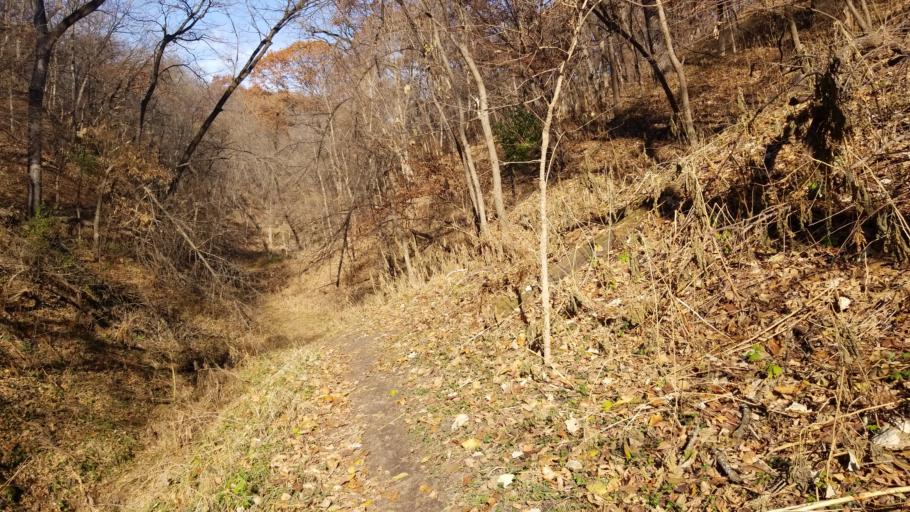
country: US
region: Nebraska
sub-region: Sarpy County
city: Bellevue
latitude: 41.1661
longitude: -95.8938
